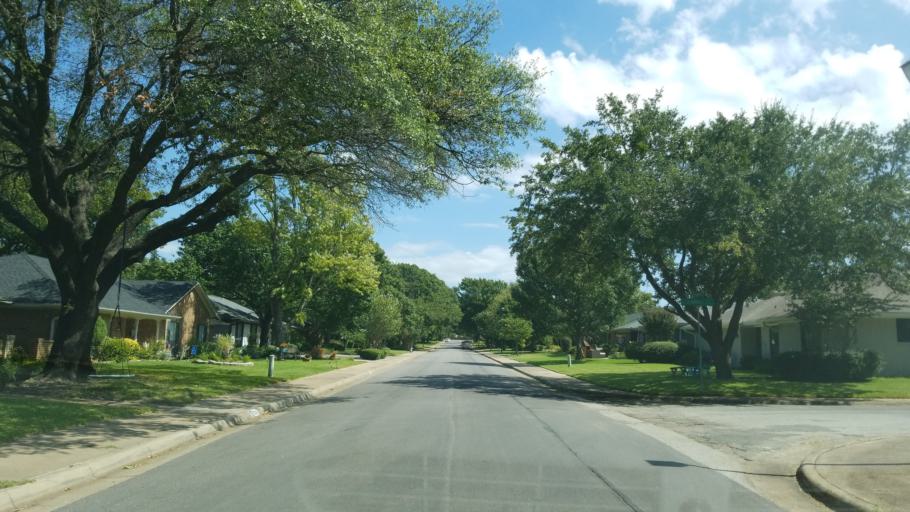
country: US
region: Texas
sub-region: Dallas County
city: Addison
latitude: 32.9671
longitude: -96.7827
